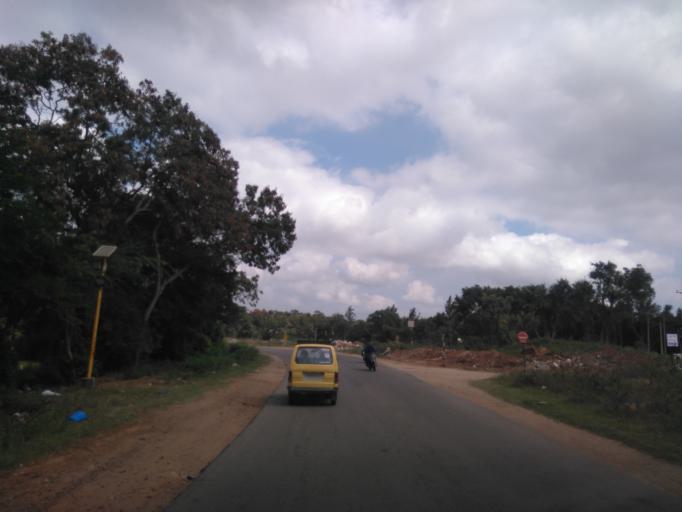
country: IN
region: Karnataka
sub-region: Mysore
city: Mysore
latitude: 12.2917
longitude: 76.7084
